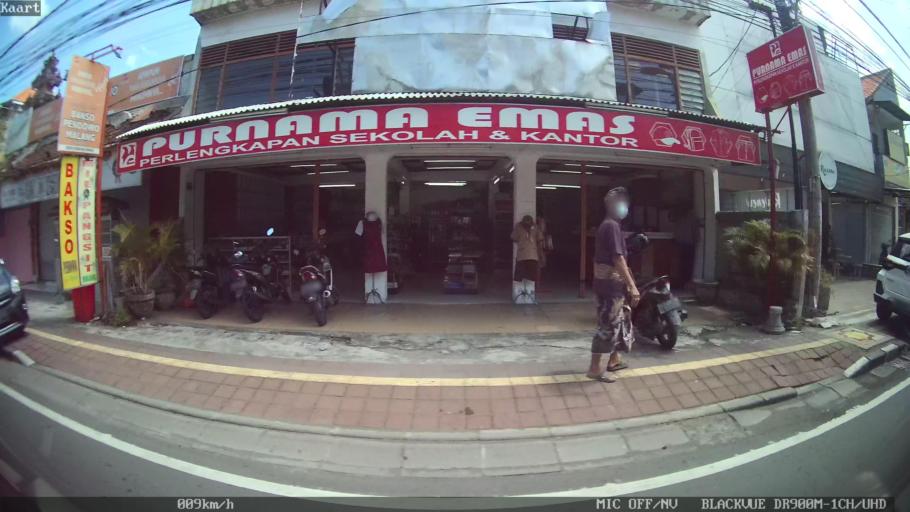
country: ID
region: Bali
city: Denpasar
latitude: -8.6653
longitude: 115.2072
